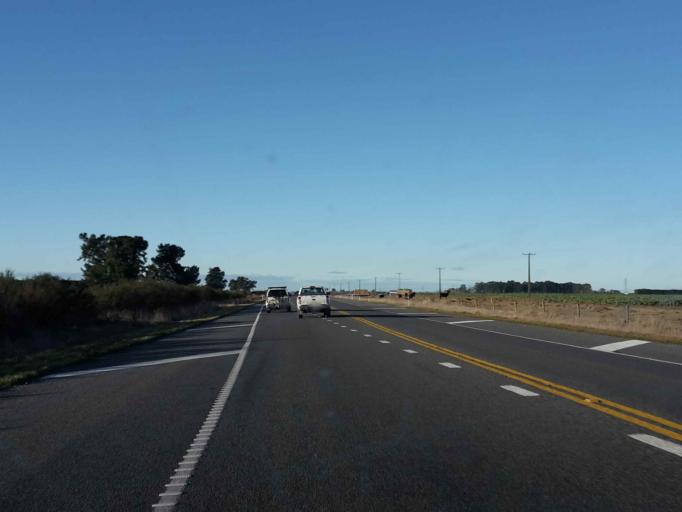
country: NZ
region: Canterbury
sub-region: Ashburton District
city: Tinwald
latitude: -44.0227
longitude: 171.5069
